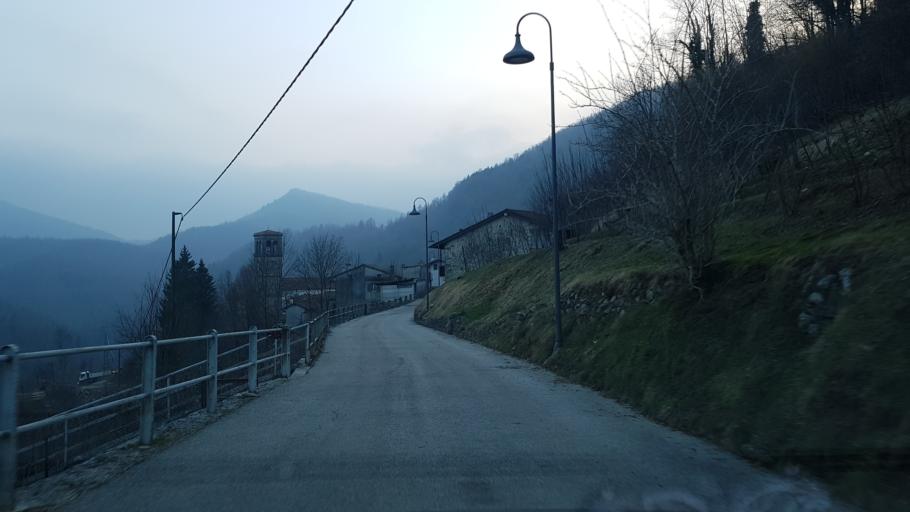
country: IT
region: Friuli Venezia Giulia
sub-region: Provincia di Udine
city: Taipana
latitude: 46.2267
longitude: 13.4062
